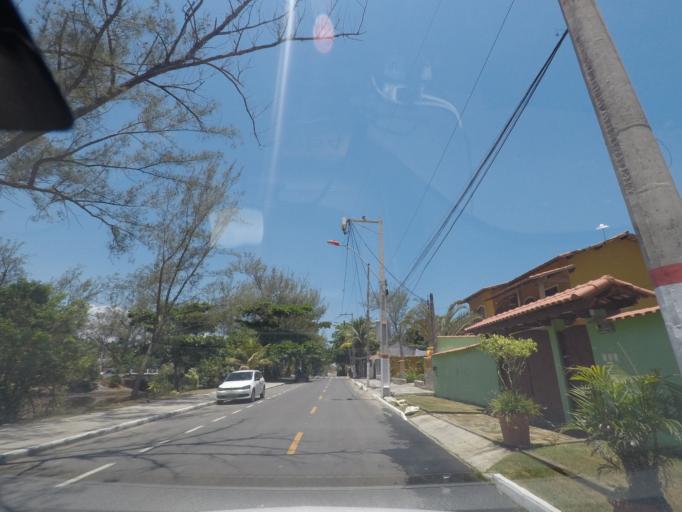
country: BR
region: Rio de Janeiro
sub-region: Niteroi
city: Niteroi
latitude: -22.9692
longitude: -43.0110
